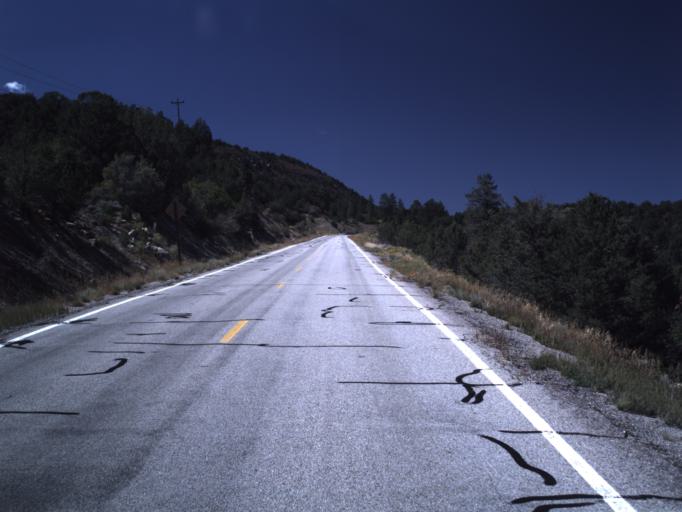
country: US
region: Utah
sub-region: Grand County
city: Moab
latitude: 38.3276
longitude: -109.1033
